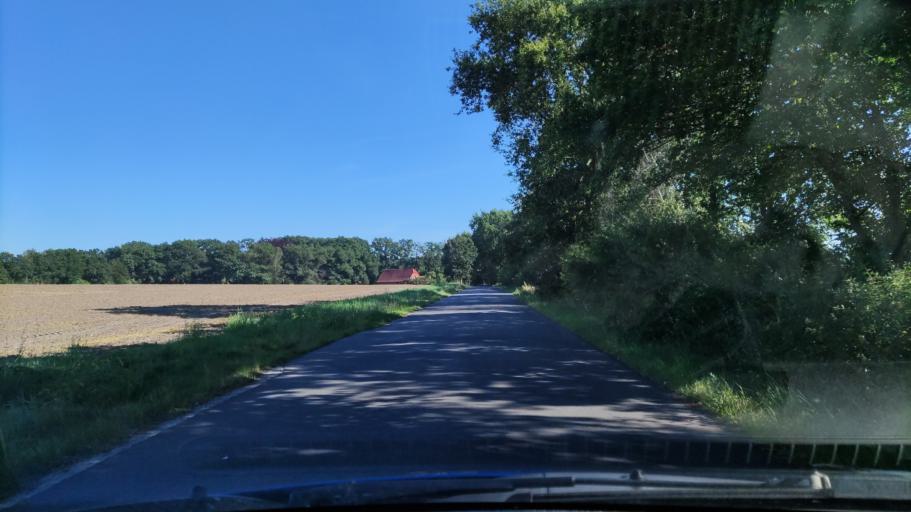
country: DE
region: Lower Saxony
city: Boitze
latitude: 53.1531
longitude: 10.7438
